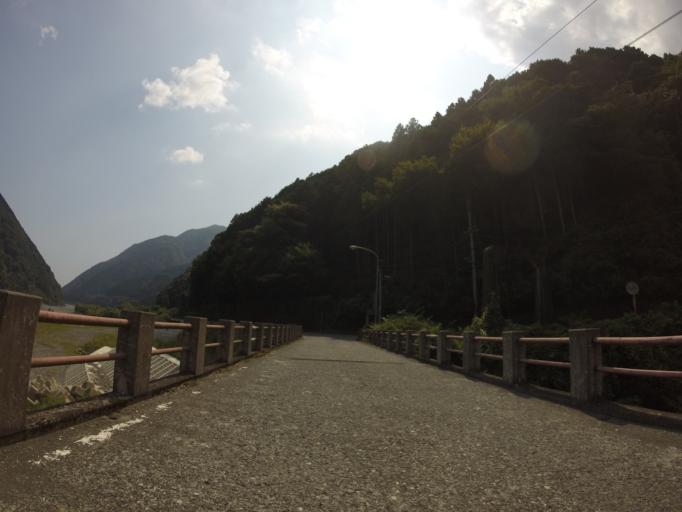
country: JP
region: Shizuoka
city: Shizuoka-shi
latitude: 35.1828
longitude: 138.3617
